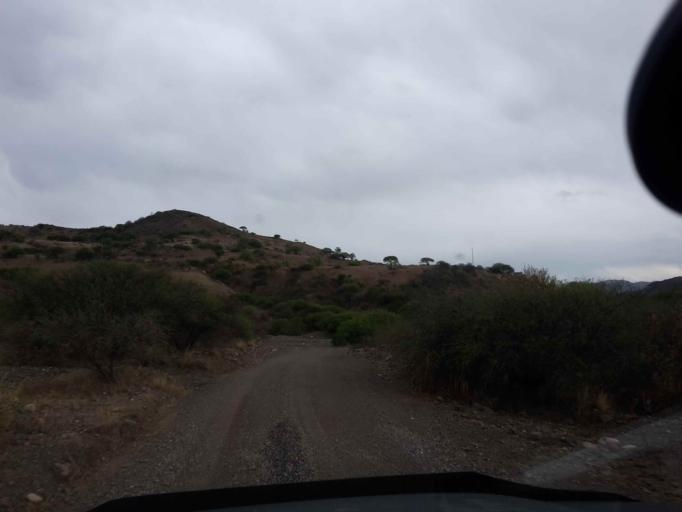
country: BO
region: Cochabamba
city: Sipe Sipe
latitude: -17.5290
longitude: -66.5178
